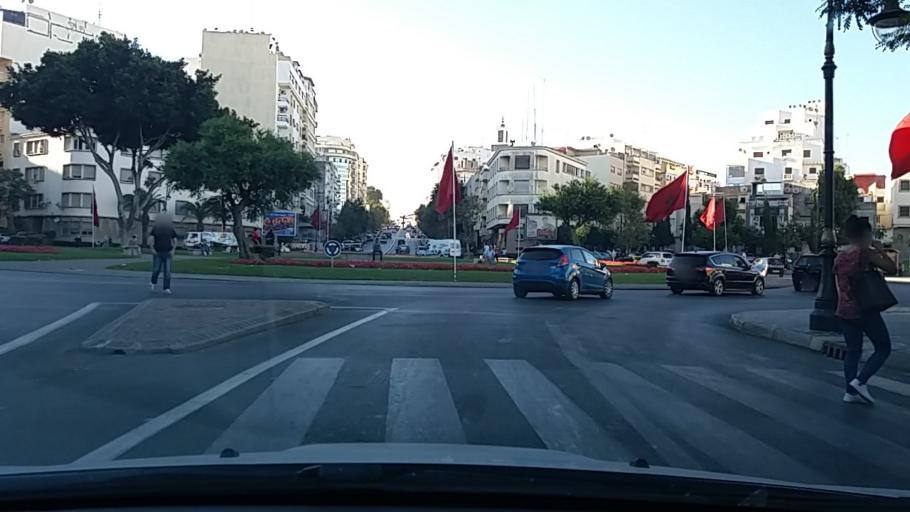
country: MA
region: Tanger-Tetouan
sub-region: Tanger-Assilah
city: Tangier
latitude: 35.7770
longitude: -5.8192
